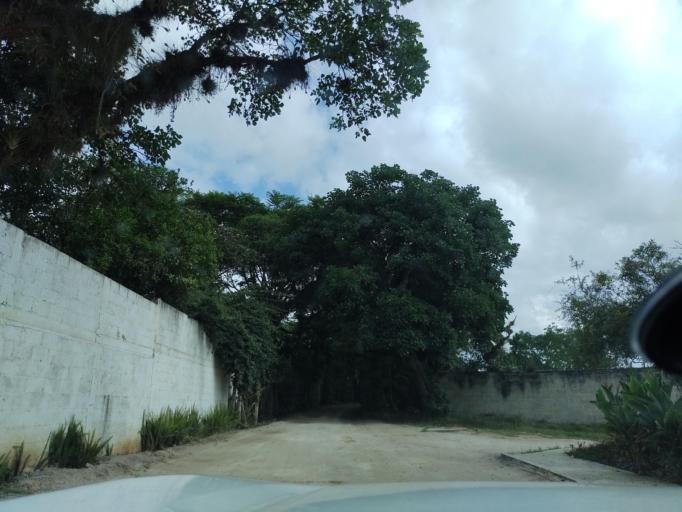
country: MX
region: Veracruz
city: Coatepec
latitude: 19.4817
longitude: -96.9366
